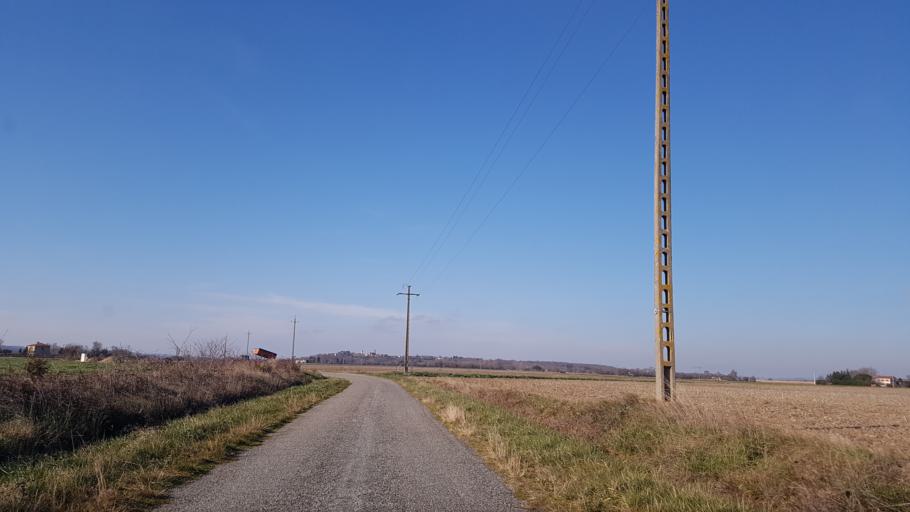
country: FR
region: Midi-Pyrenees
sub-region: Departement de l'Ariege
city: La Tour-du-Crieu
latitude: 43.1714
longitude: 1.6658
